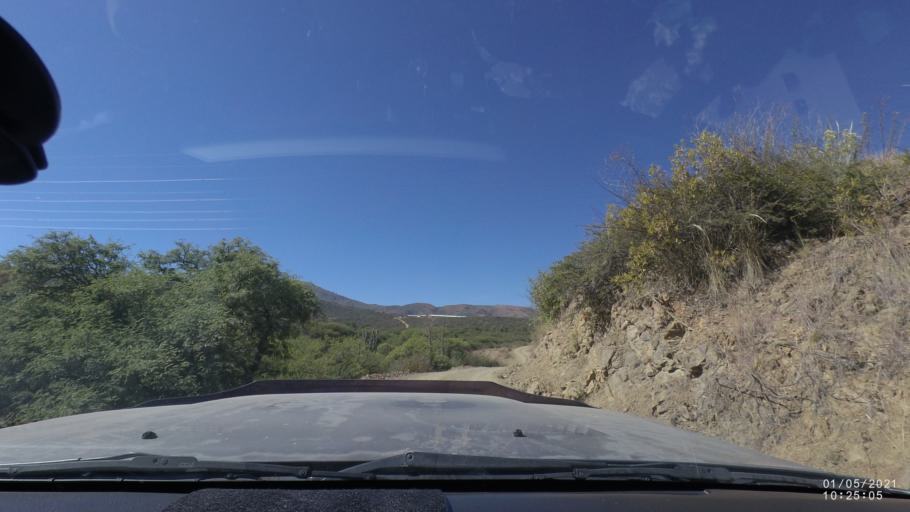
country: BO
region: Cochabamba
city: Capinota
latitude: -17.5764
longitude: -66.1943
